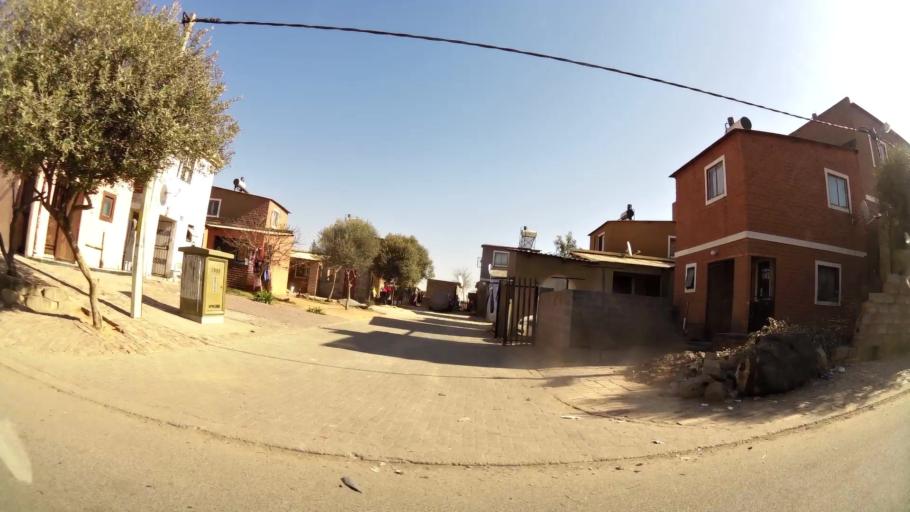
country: ZA
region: Gauteng
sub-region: City of Johannesburg Metropolitan Municipality
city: Modderfontein
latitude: -26.1074
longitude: 28.1165
